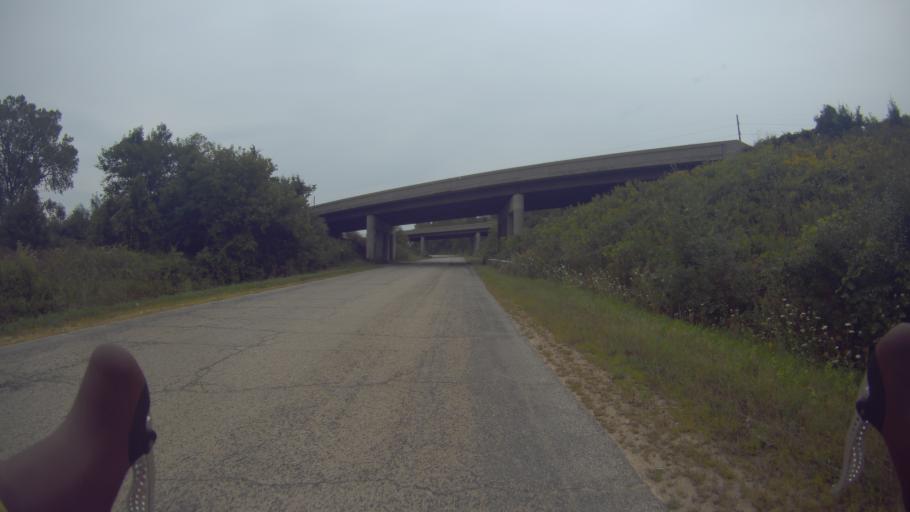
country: US
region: Wisconsin
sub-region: Jefferson County
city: Lake Mills
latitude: 43.1014
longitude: -88.9306
